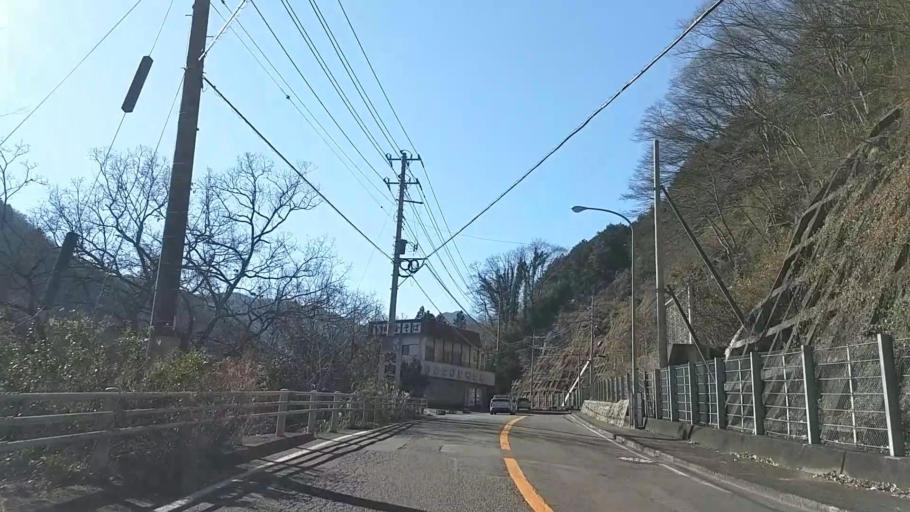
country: JP
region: Yamanashi
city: Uenohara
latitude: 35.6102
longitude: 139.0622
